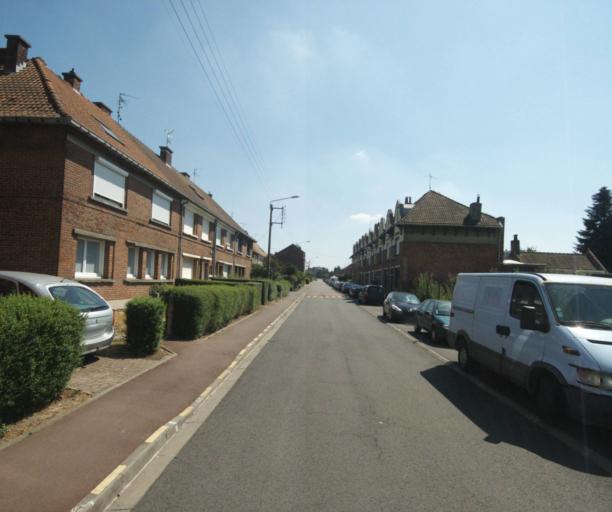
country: FR
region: Nord-Pas-de-Calais
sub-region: Departement du Nord
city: Halluin
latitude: 50.7825
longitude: 3.1135
